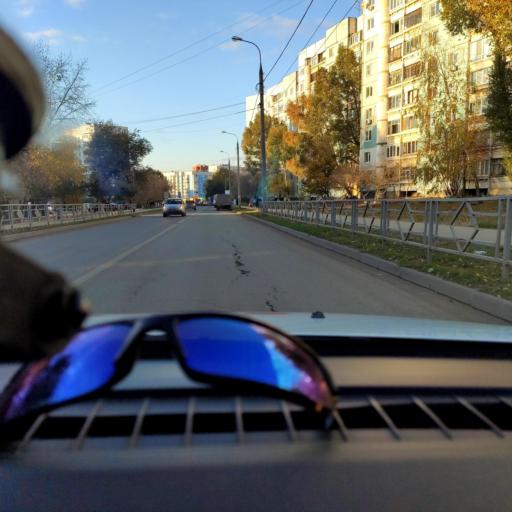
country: RU
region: Samara
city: Samara
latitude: 53.2492
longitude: 50.2097
